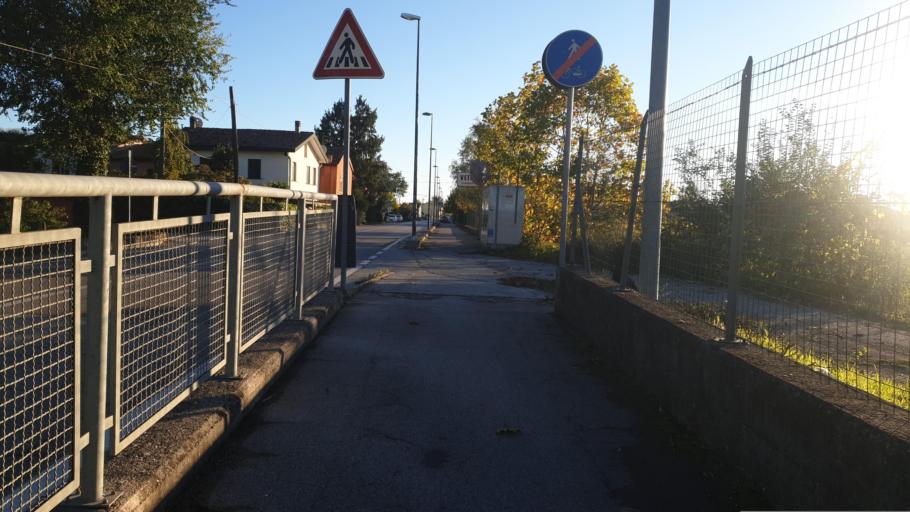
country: IT
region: Veneto
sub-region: Provincia di Venezia
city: Marano
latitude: 45.4598
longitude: 12.1065
